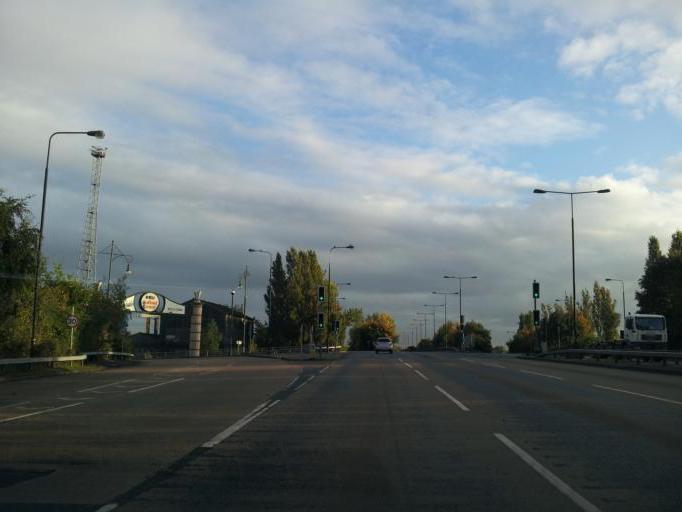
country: GB
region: England
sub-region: Trafford
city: Urmston
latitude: 53.4599
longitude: -2.3370
